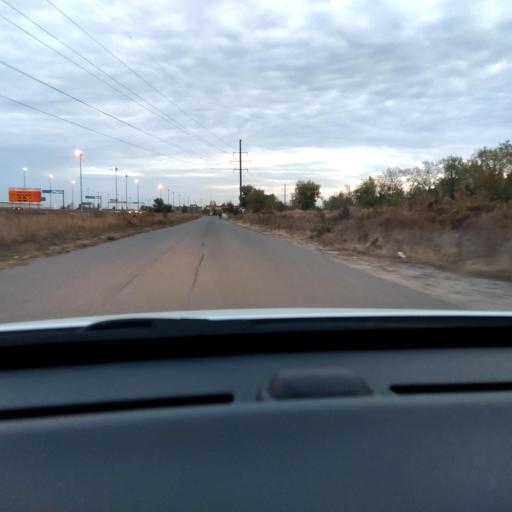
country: RU
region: Voronezj
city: Somovo
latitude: 51.6598
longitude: 39.3012
